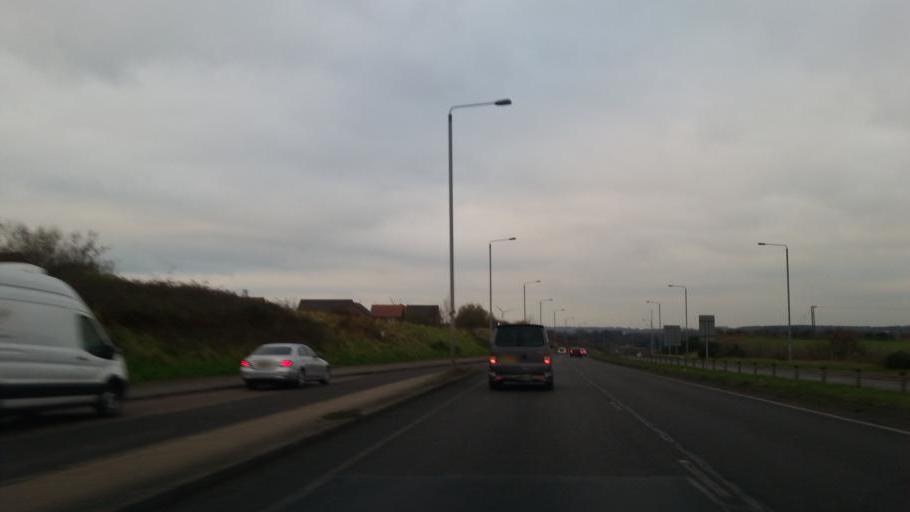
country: GB
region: England
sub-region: Nottinghamshire
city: Rainworth
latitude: 53.1206
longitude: -1.1058
